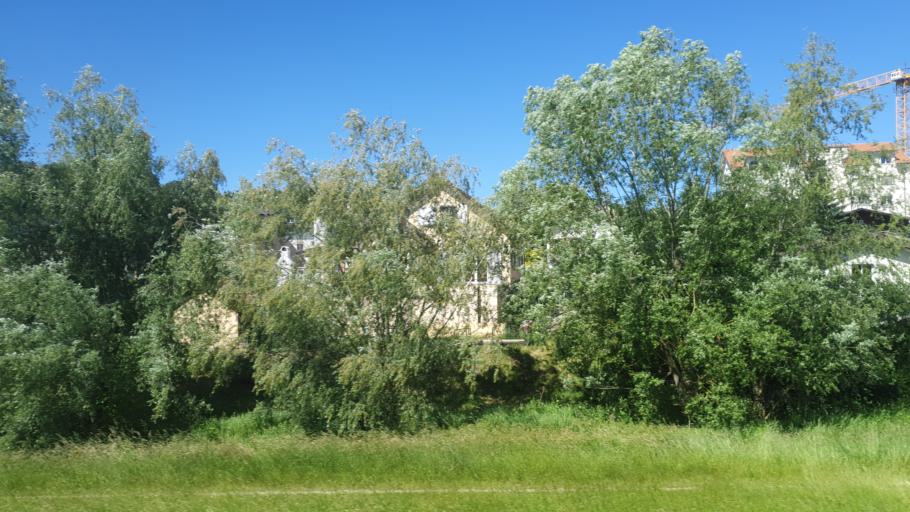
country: CH
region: Fribourg
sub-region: Sarine District
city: Belfaux
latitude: 46.8618
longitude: 7.1257
